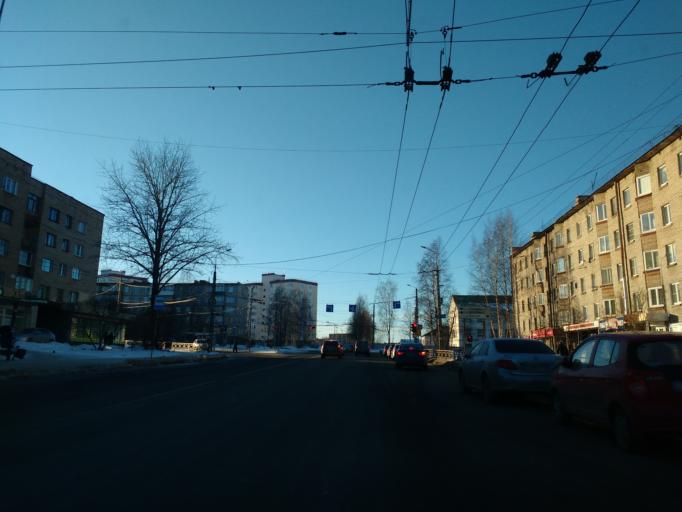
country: RU
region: Republic of Karelia
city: Petrozavodsk
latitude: 61.7740
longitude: 34.3606
